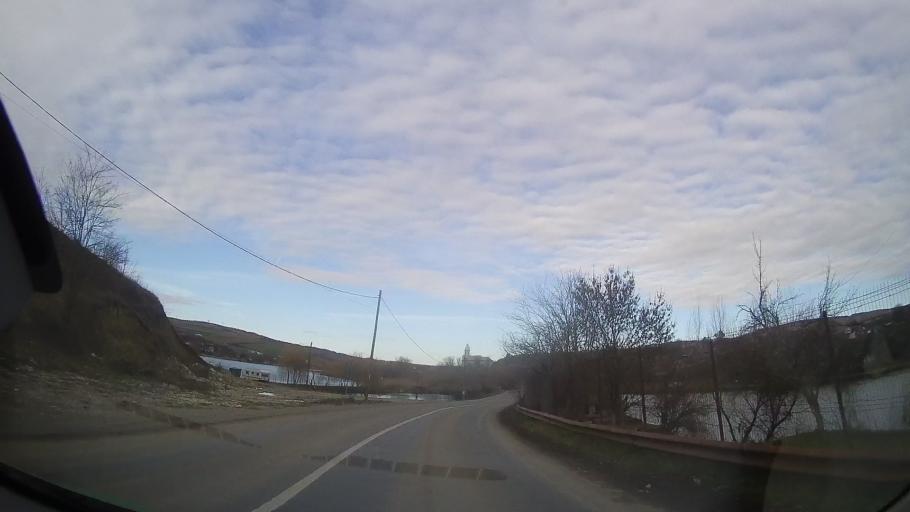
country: RO
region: Cluj
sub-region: Comuna Geaca
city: Geaca
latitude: 46.8510
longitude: 24.0920
